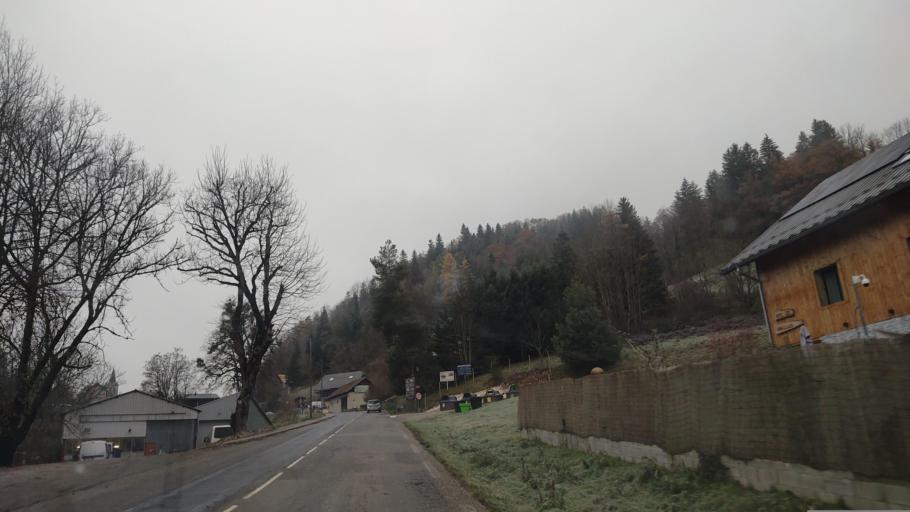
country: FR
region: Rhone-Alpes
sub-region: Departement de la Haute-Savoie
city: Doussard
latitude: 45.6784
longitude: 6.1427
